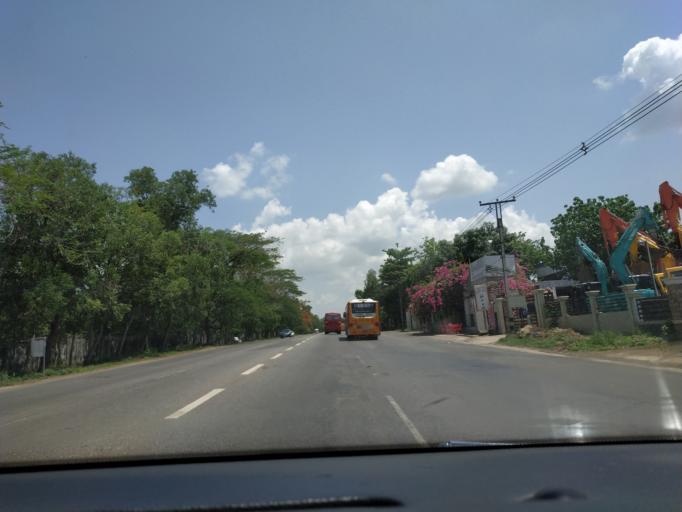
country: MM
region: Yangon
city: Yangon
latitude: 17.0005
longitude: 96.1298
